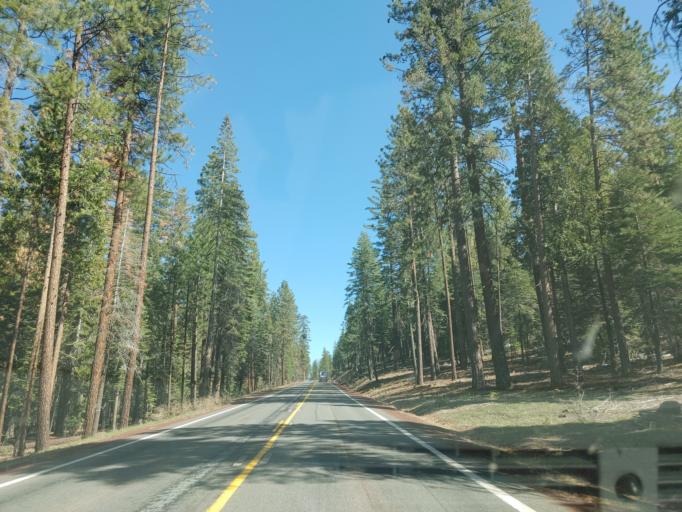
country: US
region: California
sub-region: Shasta County
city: Burney
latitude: 40.7381
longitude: -121.4605
